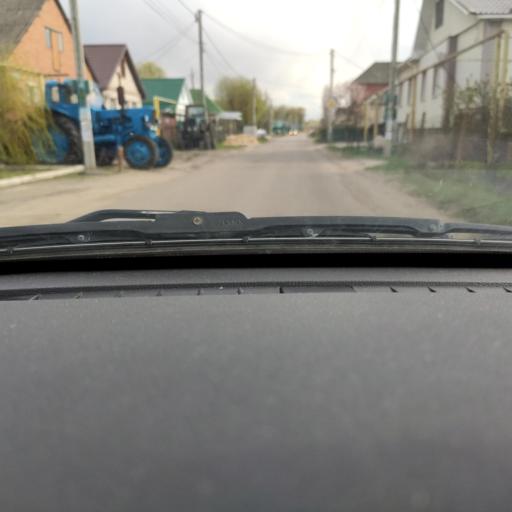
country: RU
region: Voronezj
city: Novaya Usman'
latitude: 51.6356
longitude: 39.4135
